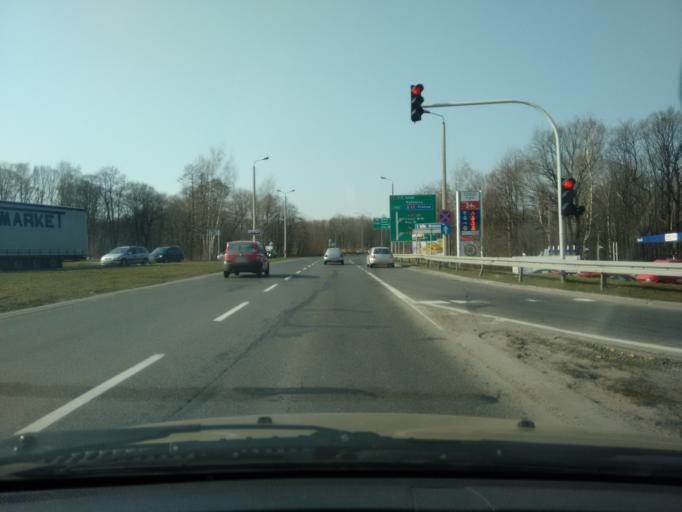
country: PL
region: Silesian Voivodeship
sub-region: Bielsko-Biala
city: Bielsko-Biala
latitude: 49.8455
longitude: 19.0333
